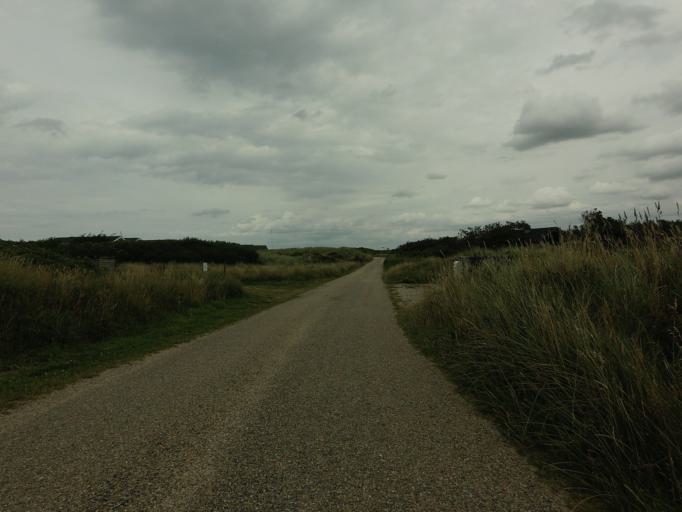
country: DK
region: North Denmark
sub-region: Jammerbugt Kommune
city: Pandrup
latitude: 57.3109
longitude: 9.6528
